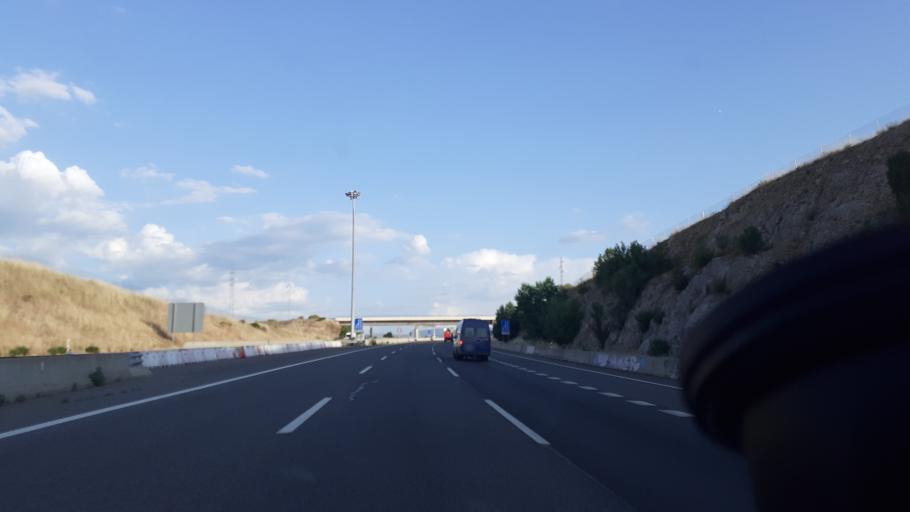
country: ES
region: Madrid
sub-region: Provincia de Madrid
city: Pedrezuela
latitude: 40.7520
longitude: -3.5909
